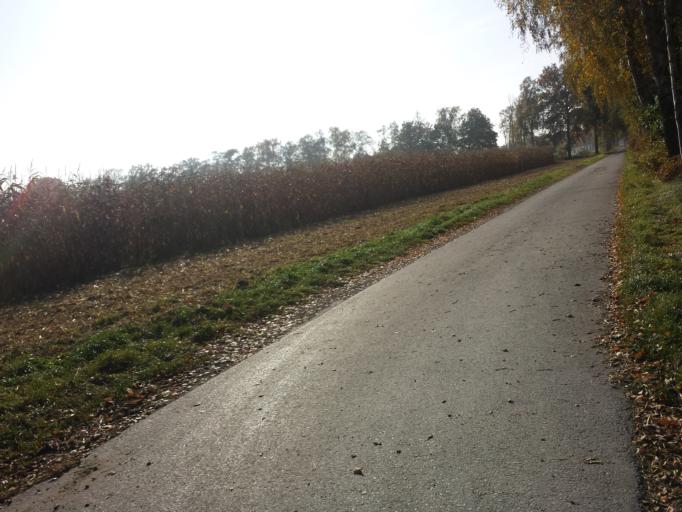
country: DE
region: North Rhine-Westphalia
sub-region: Regierungsbezirk Detmold
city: Guetersloh
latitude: 51.9312
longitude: 8.3379
